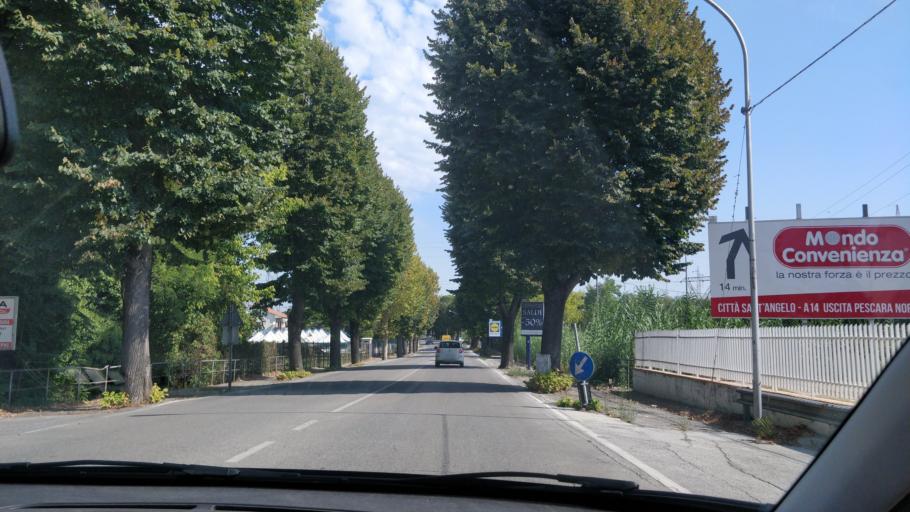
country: IT
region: Abruzzo
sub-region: Provincia di Chieti
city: Chieti
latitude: 42.3888
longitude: 14.1577
